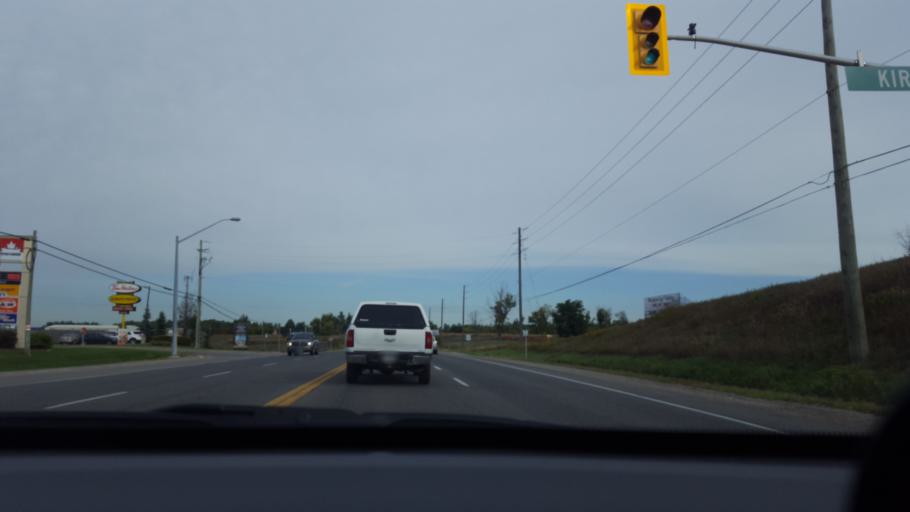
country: CA
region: Ontario
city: Vaughan
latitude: 43.8919
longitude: -79.5209
